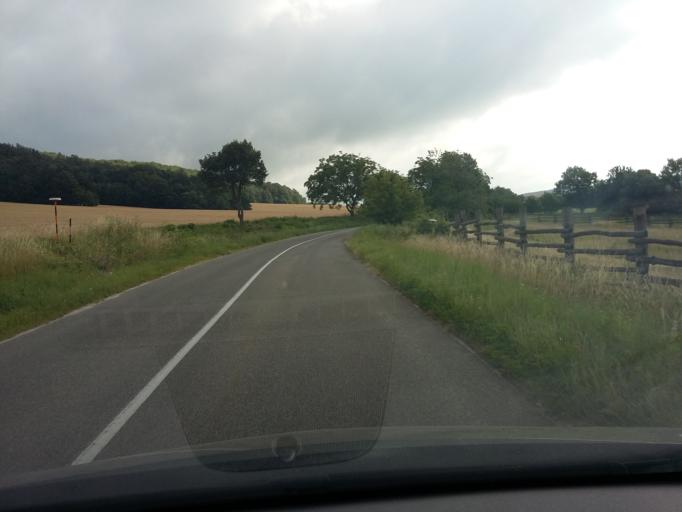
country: SK
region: Trnavsky
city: Smolenice
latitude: 48.5401
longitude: 17.3630
